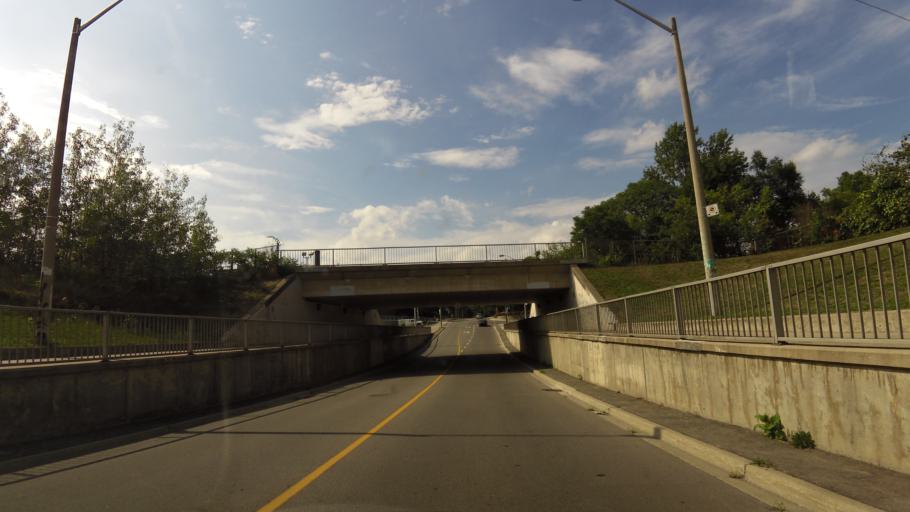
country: CA
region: Ontario
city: Etobicoke
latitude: 43.6497
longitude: -79.5202
